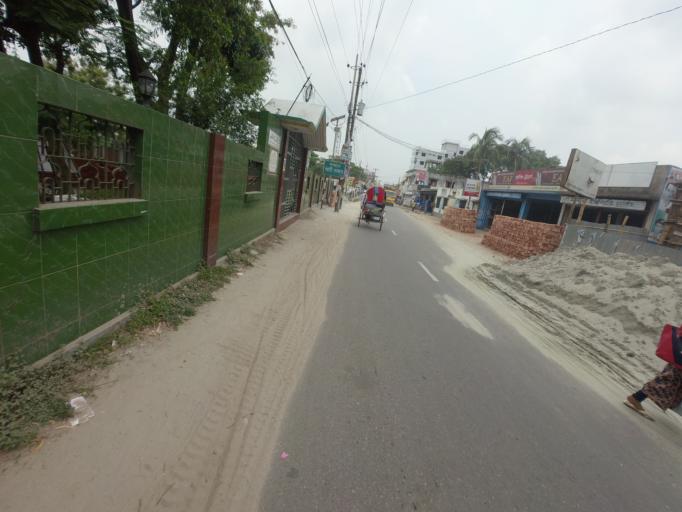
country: BD
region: Dhaka
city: Azimpur
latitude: 23.7290
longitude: 90.3374
